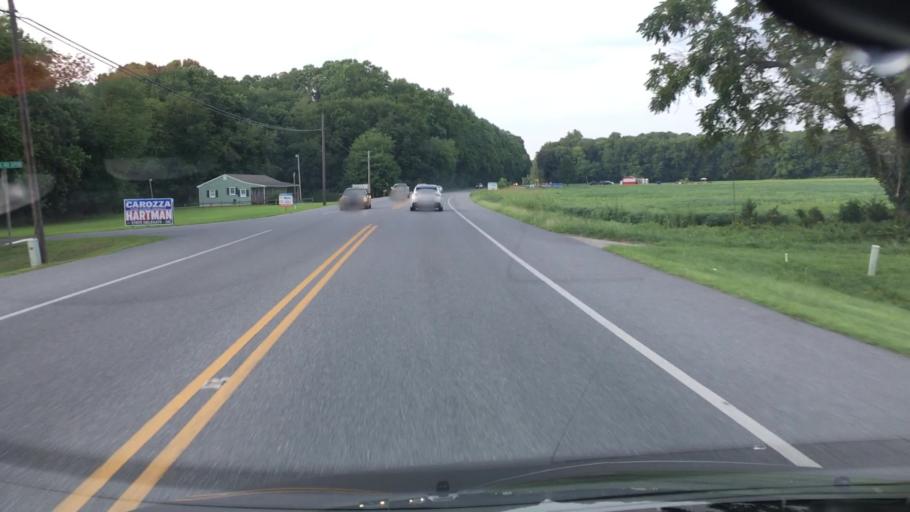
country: US
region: Maryland
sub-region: Worcester County
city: Ocean Pines
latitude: 38.3616
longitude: -75.1684
